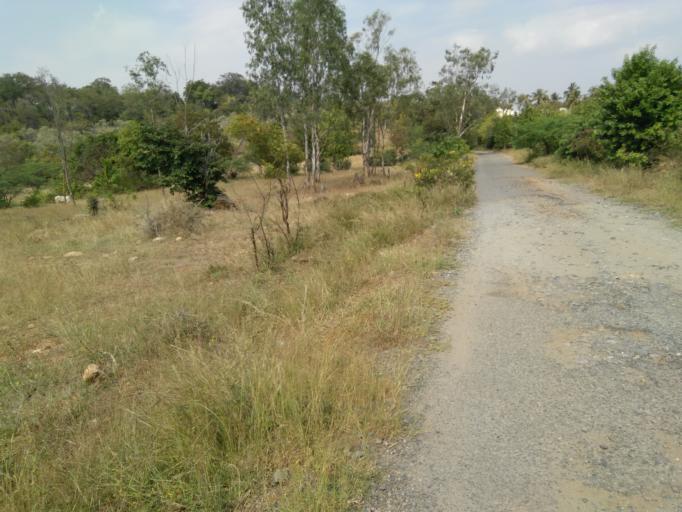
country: IN
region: Tamil Nadu
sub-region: Coimbatore
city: Karamadai
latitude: 11.2616
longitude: 77.0116
